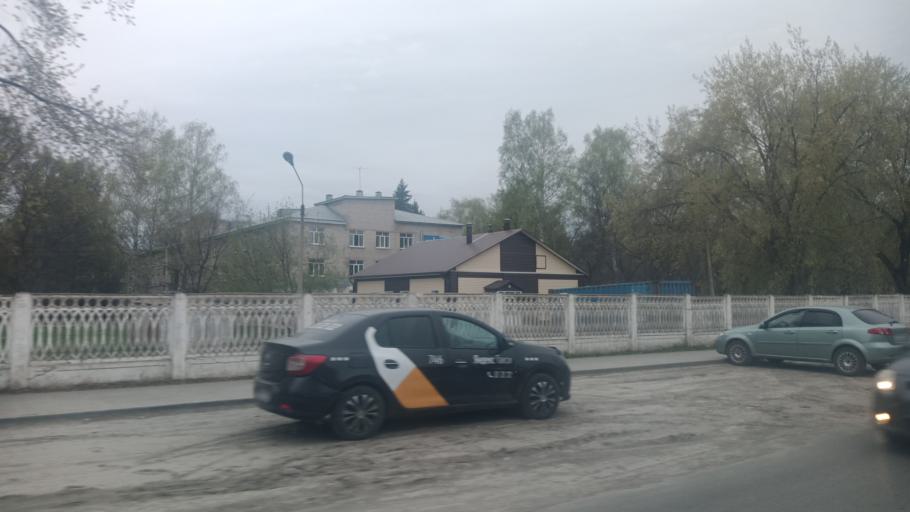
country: RU
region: Altai Krai
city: Yuzhnyy
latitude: 53.2541
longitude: 83.6847
